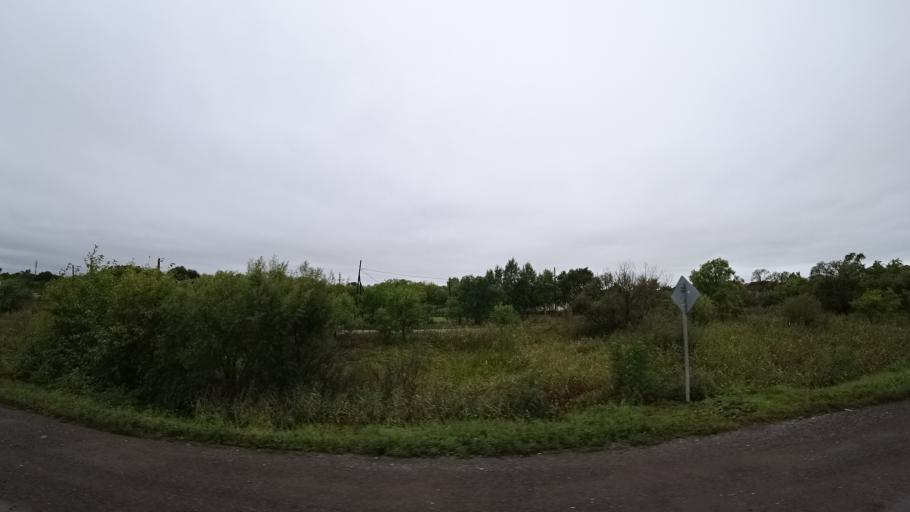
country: RU
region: Primorskiy
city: Monastyrishche
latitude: 44.2139
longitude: 132.4497
